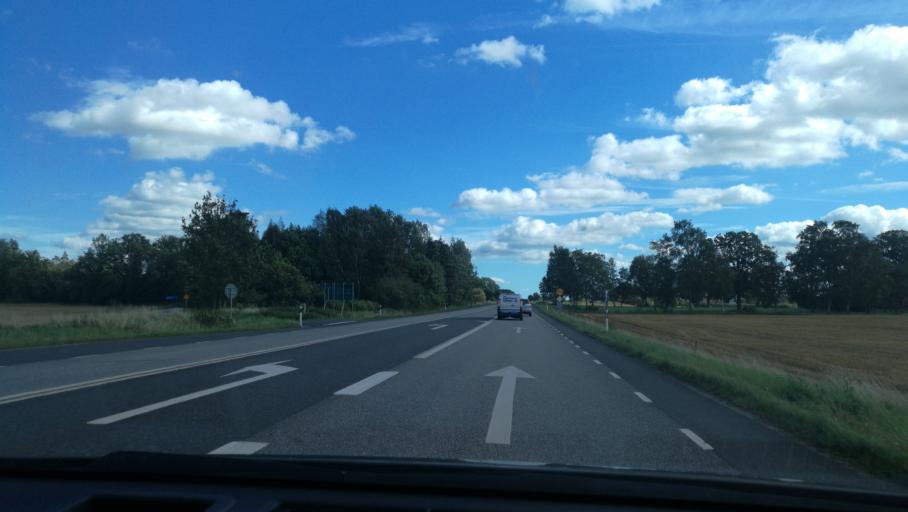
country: SE
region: Vaestra Goetaland
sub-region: Gotene Kommun
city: Kallby
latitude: 58.5115
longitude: 13.3463
